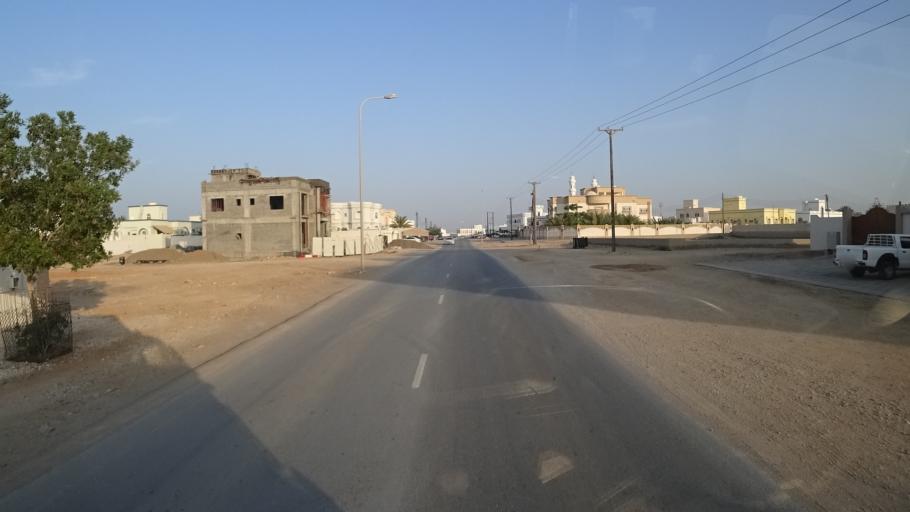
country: OM
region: Ash Sharqiyah
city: Sur
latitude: 22.6137
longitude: 59.4635
